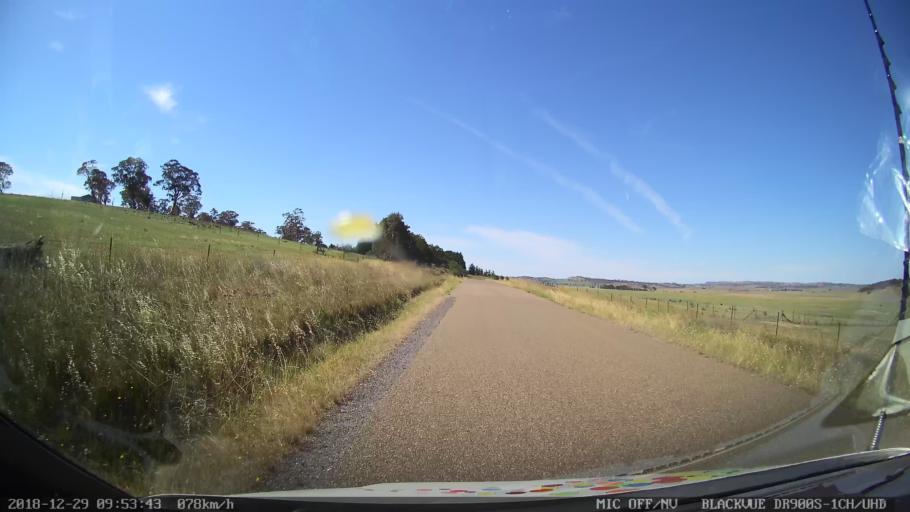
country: AU
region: New South Wales
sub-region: Goulburn Mulwaree
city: Goulburn
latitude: -34.7549
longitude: 149.4687
